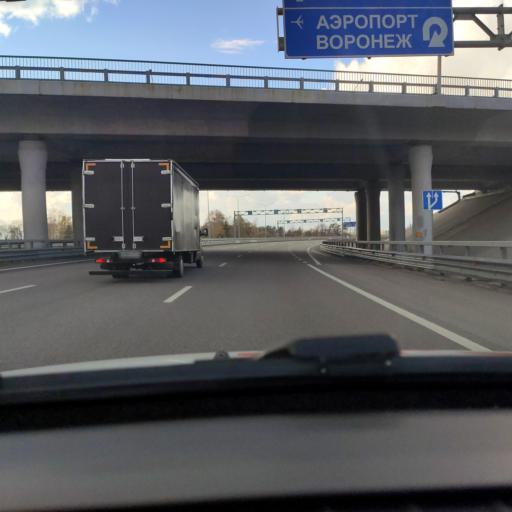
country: RU
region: Voronezj
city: Podgornoye
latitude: 51.8386
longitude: 39.2192
